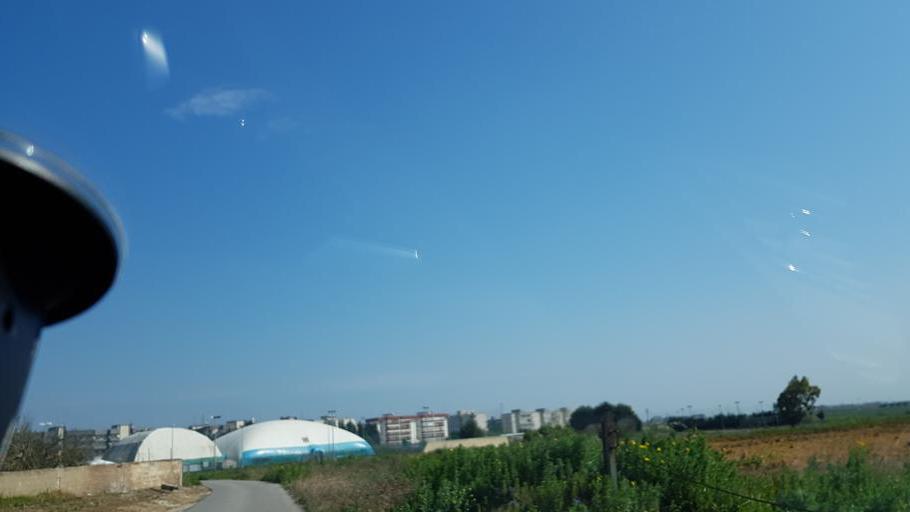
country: IT
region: Apulia
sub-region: Provincia di Brindisi
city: Brindisi
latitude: 40.6145
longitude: 17.9307
